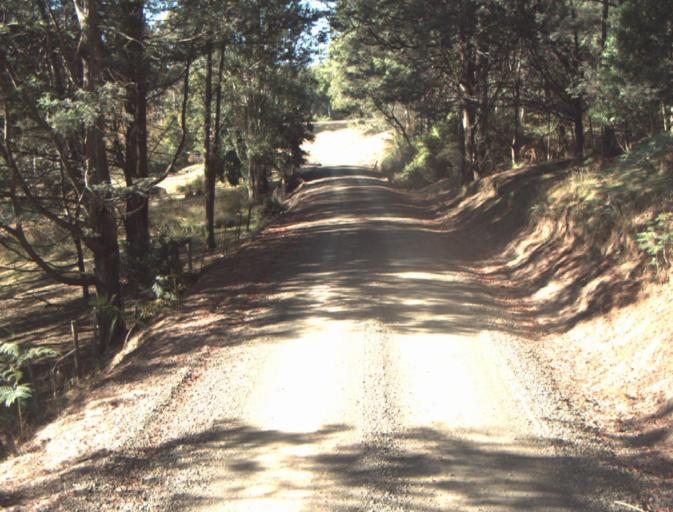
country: AU
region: Tasmania
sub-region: Launceston
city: Mayfield
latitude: -41.2975
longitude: 147.1980
